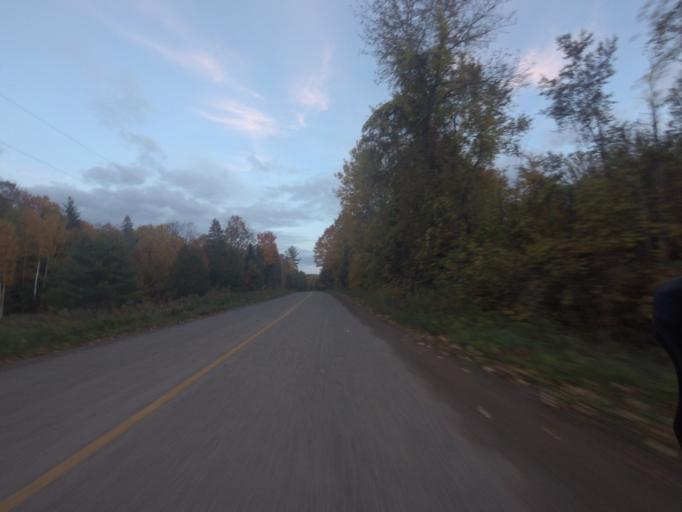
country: CA
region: Ontario
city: Renfrew
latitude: 45.3520
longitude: -76.9497
